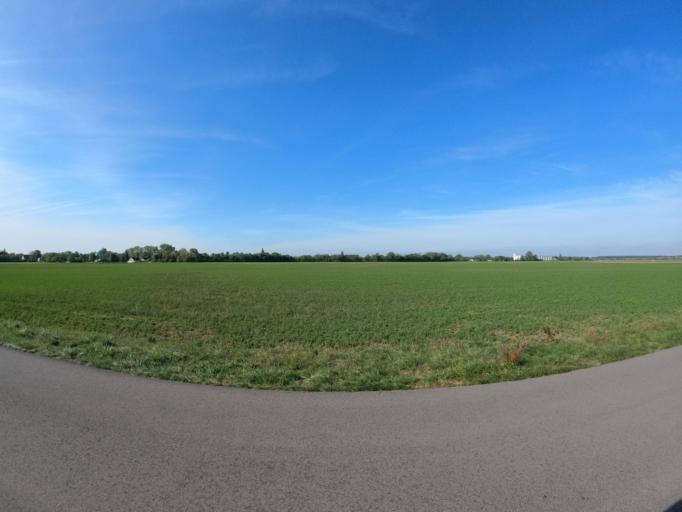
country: FR
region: Franche-Comte
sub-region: Departement du Jura
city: Bletterans
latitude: 46.7496
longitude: 5.4885
